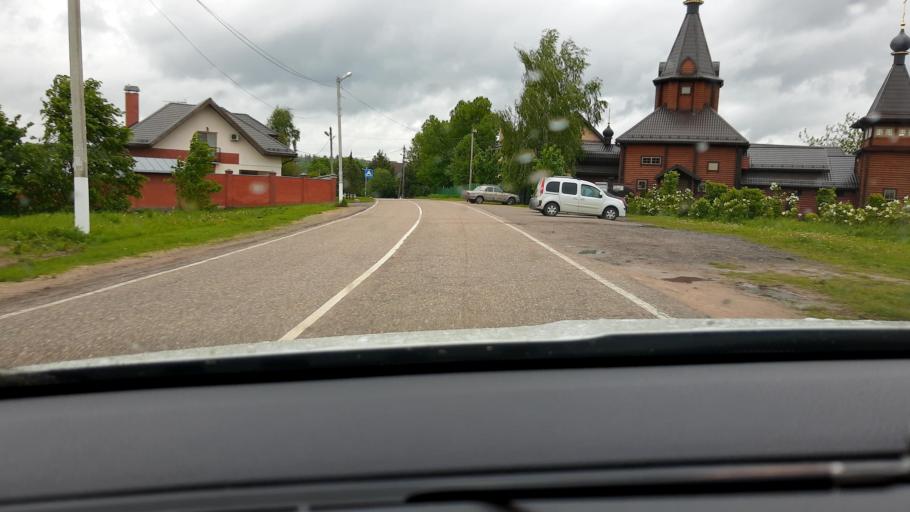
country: RU
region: Moskovskaya
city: Zvenigorod
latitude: 55.7315
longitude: 36.9203
